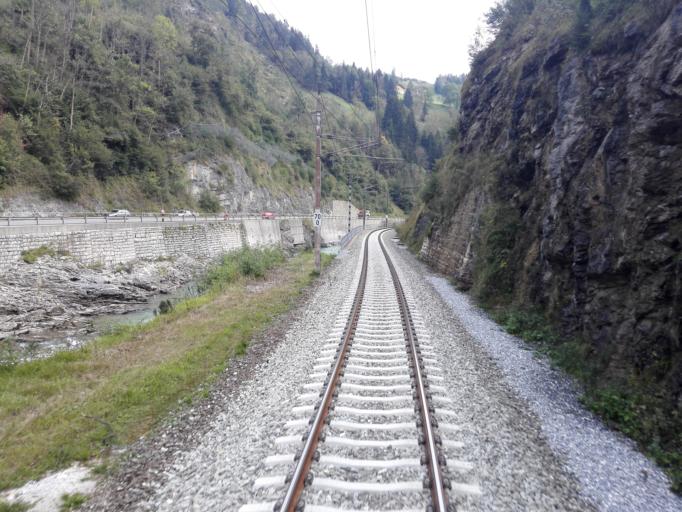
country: AT
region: Salzburg
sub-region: Politischer Bezirk Sankt Johann im Pongau
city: Goldegg
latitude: 47.3085
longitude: 13.1152
